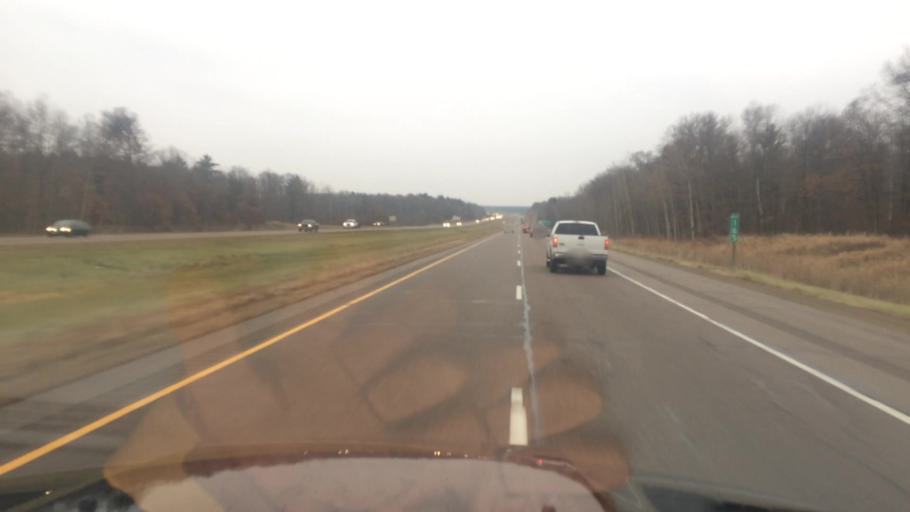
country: US
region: Wisconsin
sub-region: Portage County
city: Stevens Point
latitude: 44.5906
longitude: -89.6114
